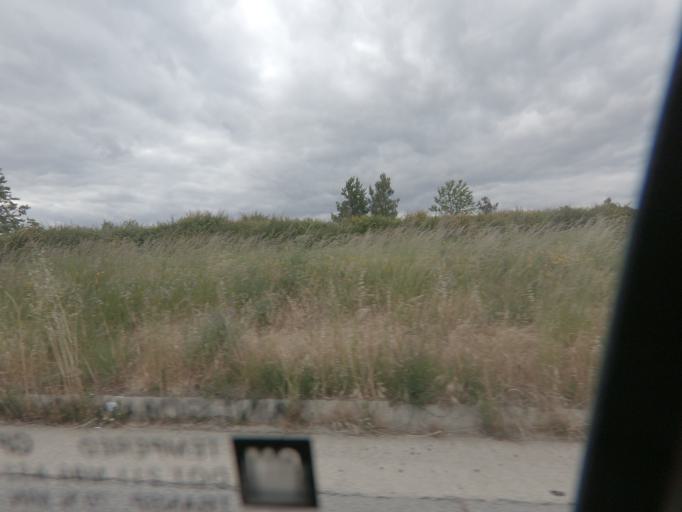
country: PT
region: Vila Real
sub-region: Sabrosa
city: Vilela
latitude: 41.2625
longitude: -7.6161
